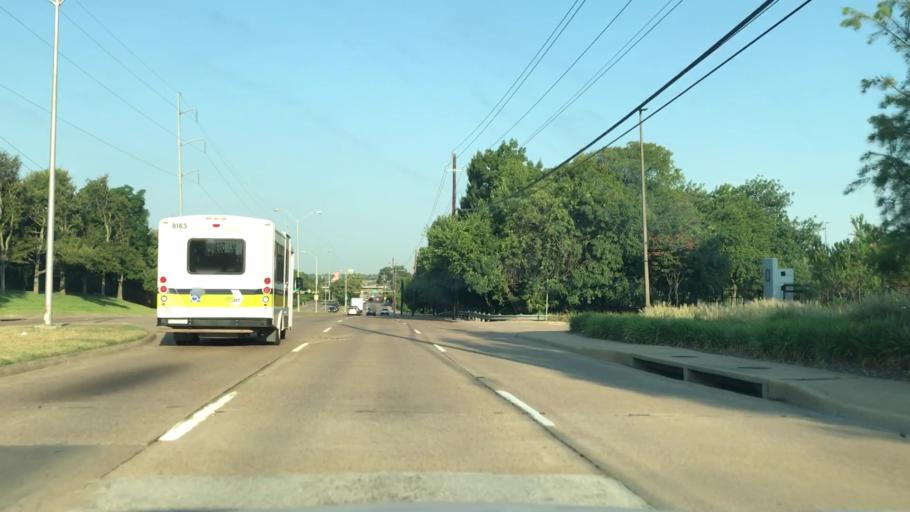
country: US
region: Texas
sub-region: Dallas County
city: Richardson
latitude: 32.9093
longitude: -96.7563
